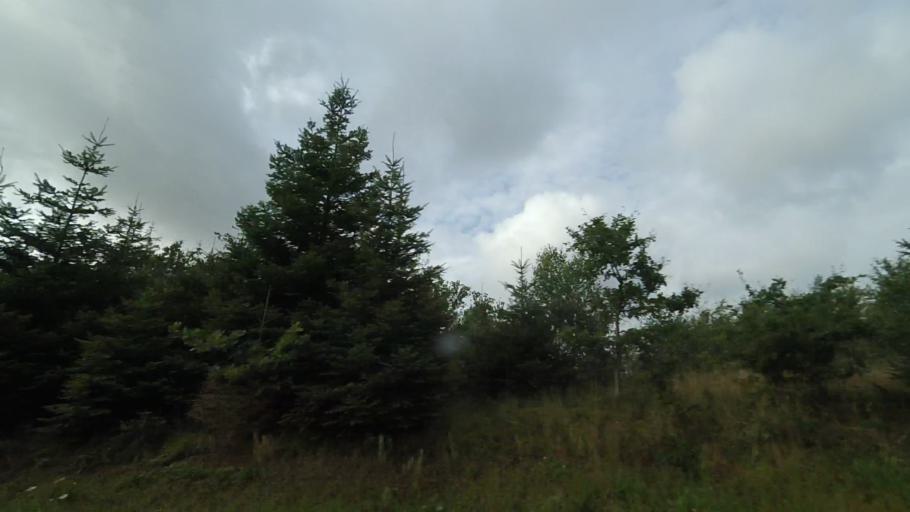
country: DK
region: Central Jutland
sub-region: Syddjurs Kommune
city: Ryomgard
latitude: 56.3581
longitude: 10.5175
